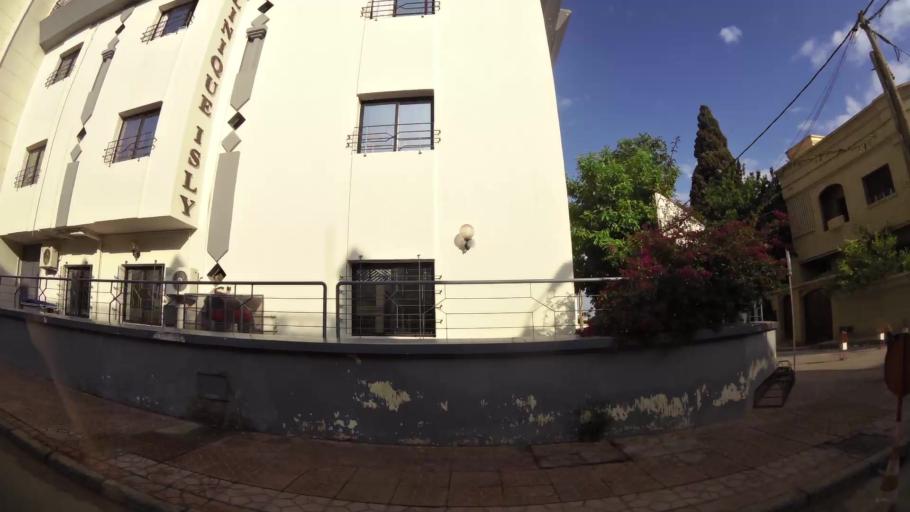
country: MA
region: Oriental
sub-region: Oujda-Angad
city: Oujda
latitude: 34.6731
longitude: -1.9255
